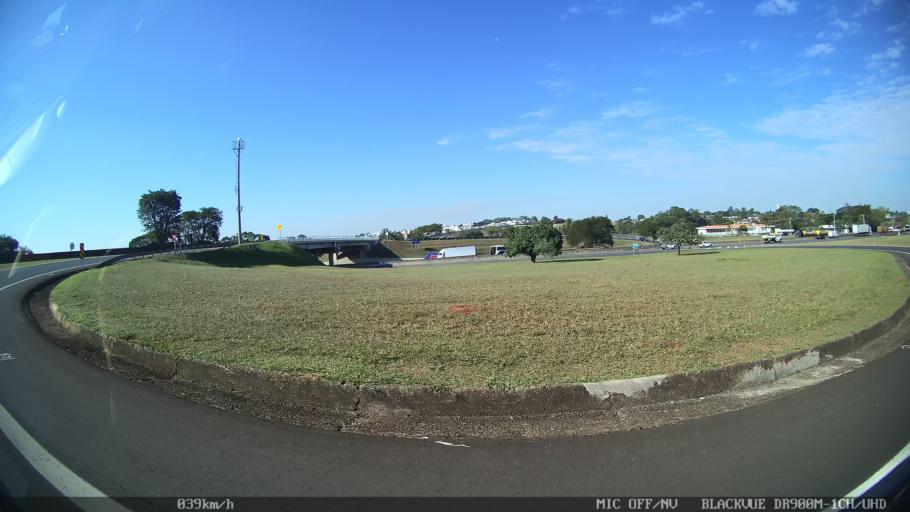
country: BR
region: Sao Paulo
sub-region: Americana
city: Americana
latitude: -22.7288
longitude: -47.2927
